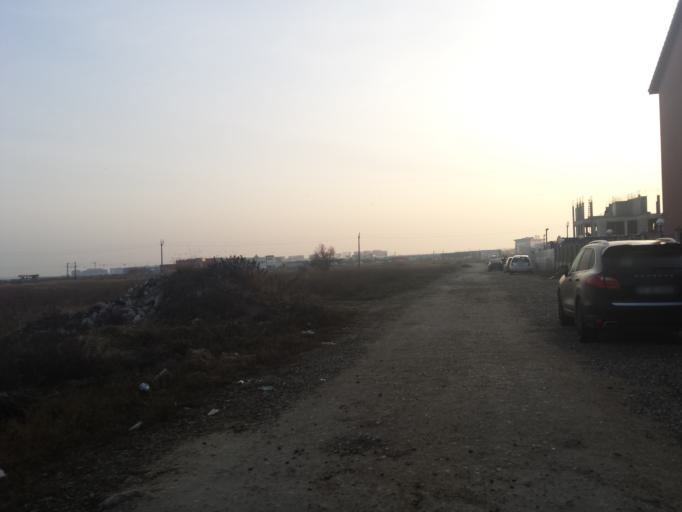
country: RO
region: Ilfov
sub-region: Comuna Tunari
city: Tunari
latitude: 44.5302
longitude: 26.1484
